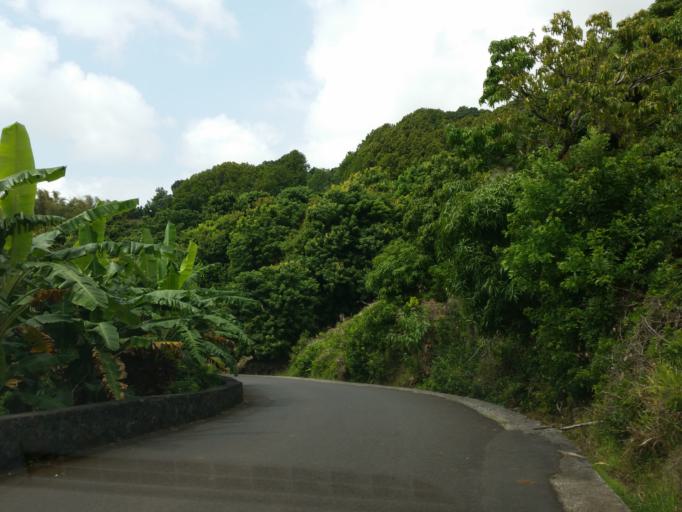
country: RE
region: Reunion
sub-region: Reunion
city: Sainte-Suzanne
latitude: -20.9259
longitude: 55.6058
